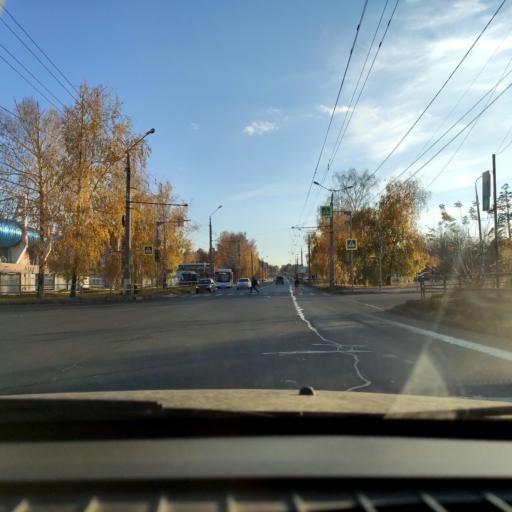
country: RU
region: Samara
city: Tol'yatti
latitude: 53.5014
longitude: 49.3900
